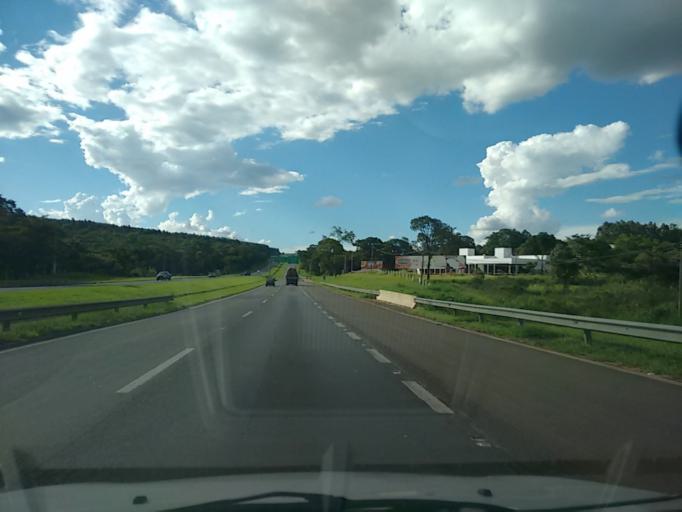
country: BR
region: Sao Paulo
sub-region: Sao Carlos
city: Sao Carlos
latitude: -22.0680
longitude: -47.8470
